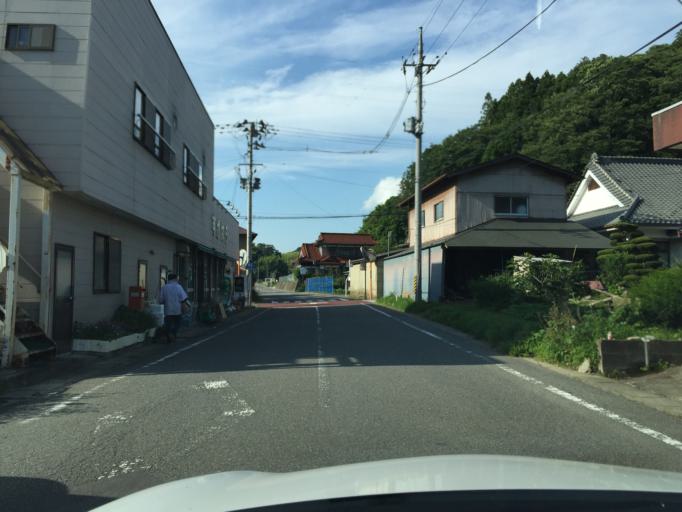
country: JP
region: Fukushima
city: Miharu
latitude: 37.3505
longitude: 140.5109
